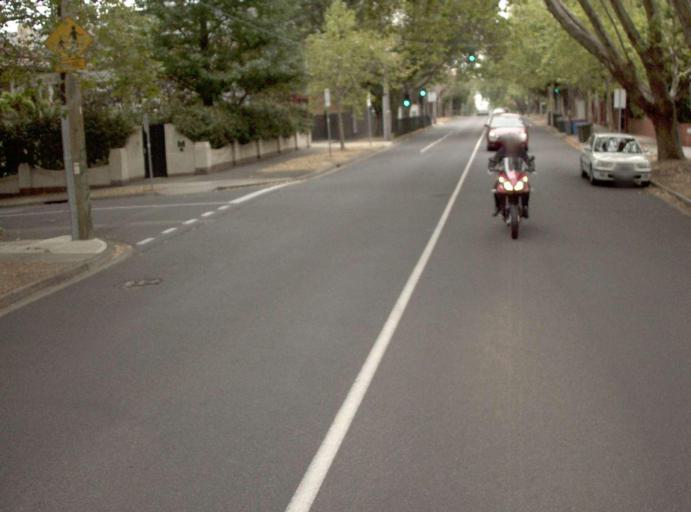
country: AU
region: Victoria
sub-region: Port Phillip
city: St Kilda East
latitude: -37.8576
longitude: 145.0110
